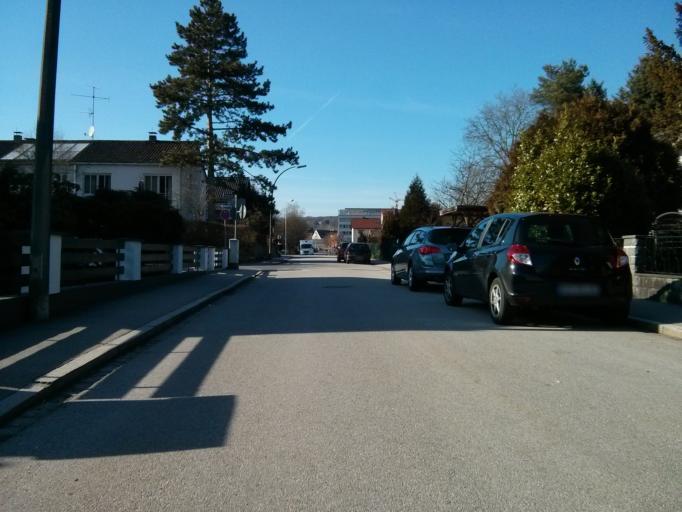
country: DE
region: Bavaria
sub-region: Lower Bavaria
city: Deggendorf
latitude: 48.8384
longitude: 12.9563
